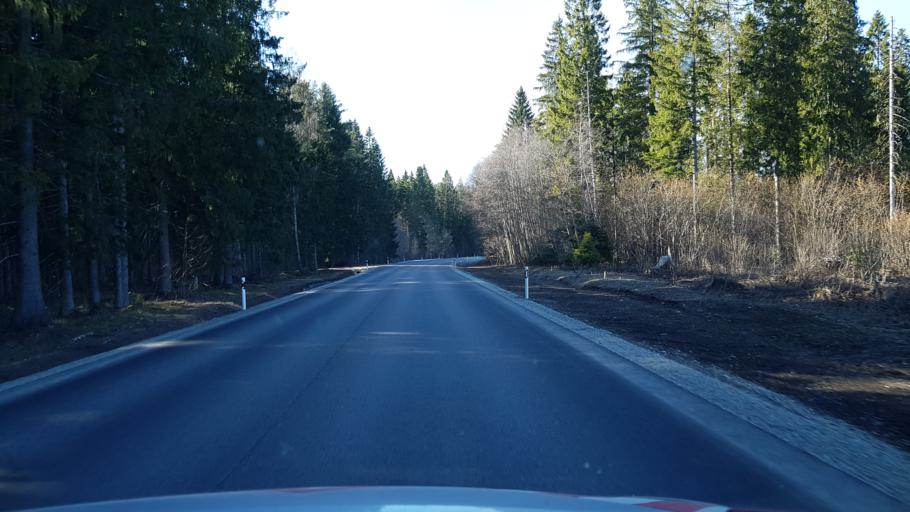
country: EE
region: Laeaene-Virumaa
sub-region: Vinni vald
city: Vinni
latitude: 59.1331
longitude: 26.6022
